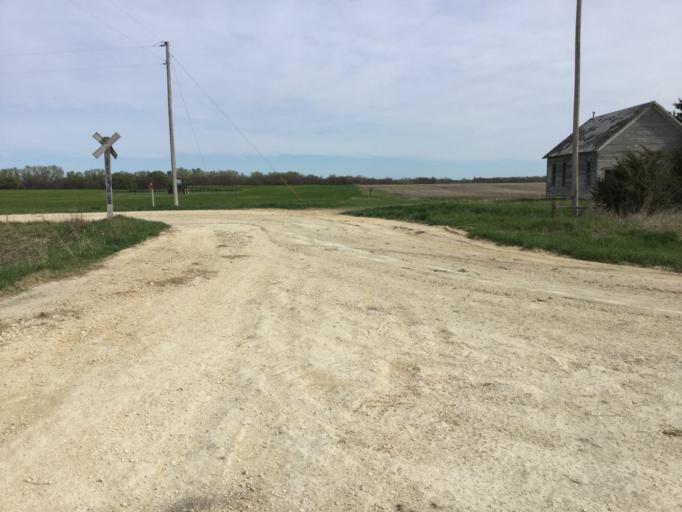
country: US
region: Kansas
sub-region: Osborne County
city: Osborne
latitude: 39.4157
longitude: -98.5643
